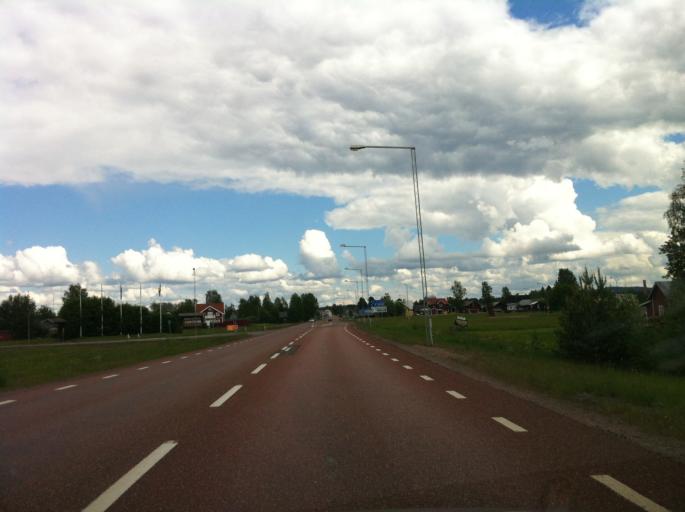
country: SE
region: Dalarna
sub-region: Malung-Saelens kommun
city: Malung
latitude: 60.6785
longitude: 13.7024
